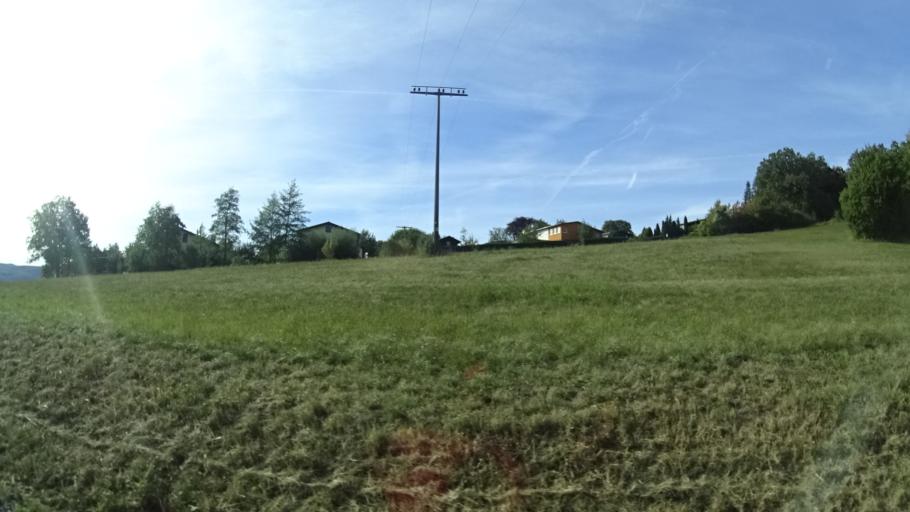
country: DE
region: Bavaria
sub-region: Regierungsbezirk Unterfranken
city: Fladungen
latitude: 50.5259
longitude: 10.1557
